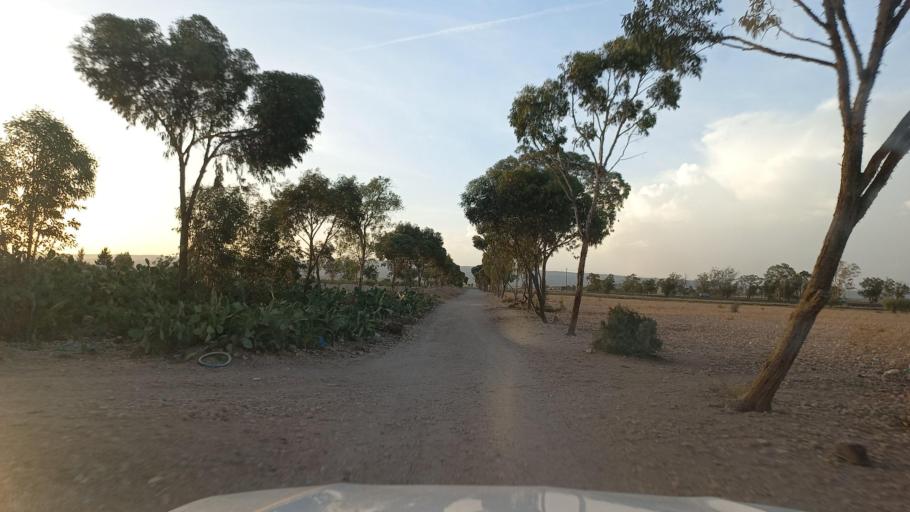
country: TN
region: Al Qasrayn
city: Kasserine
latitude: 35.2404
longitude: 8.9938
